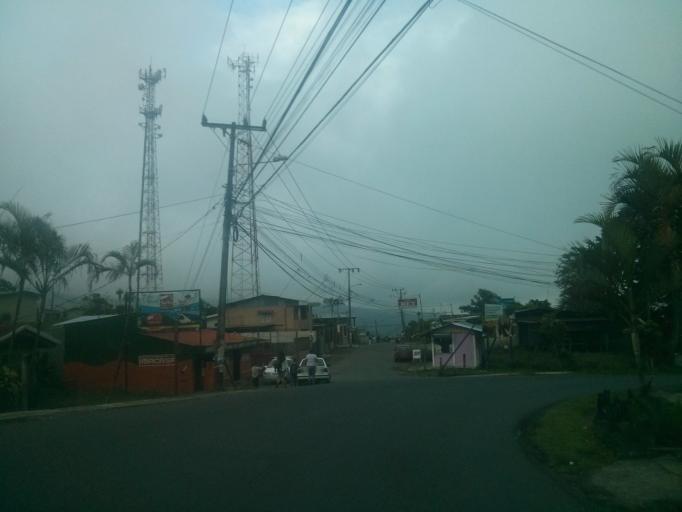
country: CR
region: Cartago
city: Cot
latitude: 9.8866
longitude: -83.8073
